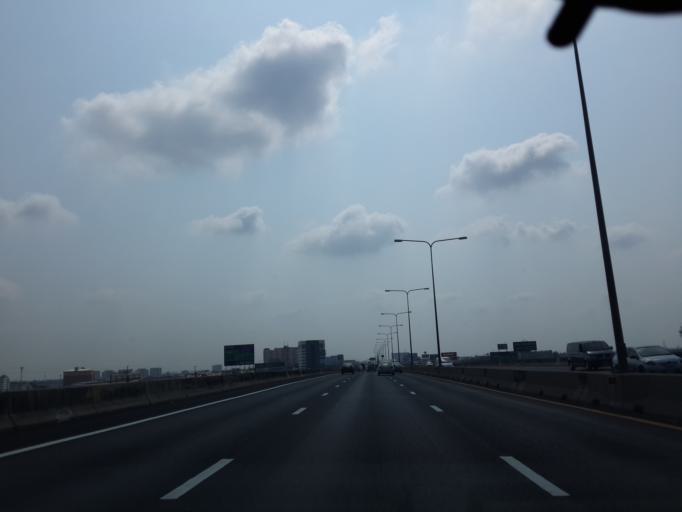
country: TH
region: Bangkok
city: Bang Na
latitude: 13.6392
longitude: 100.7015
